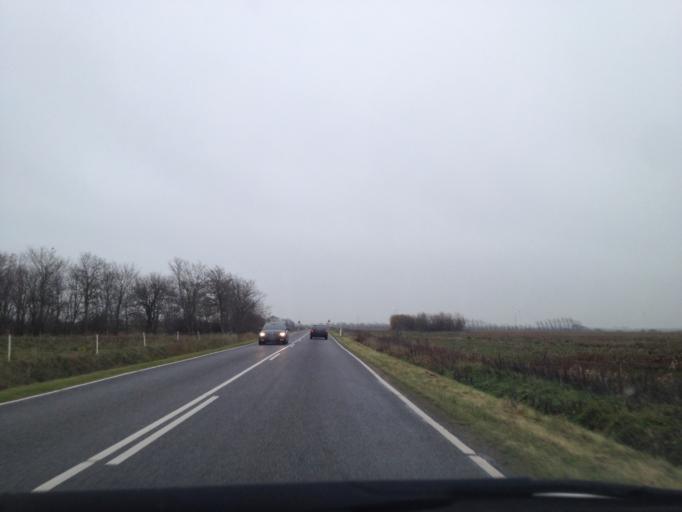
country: DK
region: South Denmark
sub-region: Tonder Kommune
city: Sherrebek
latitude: 55.0722
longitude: 8.7285
